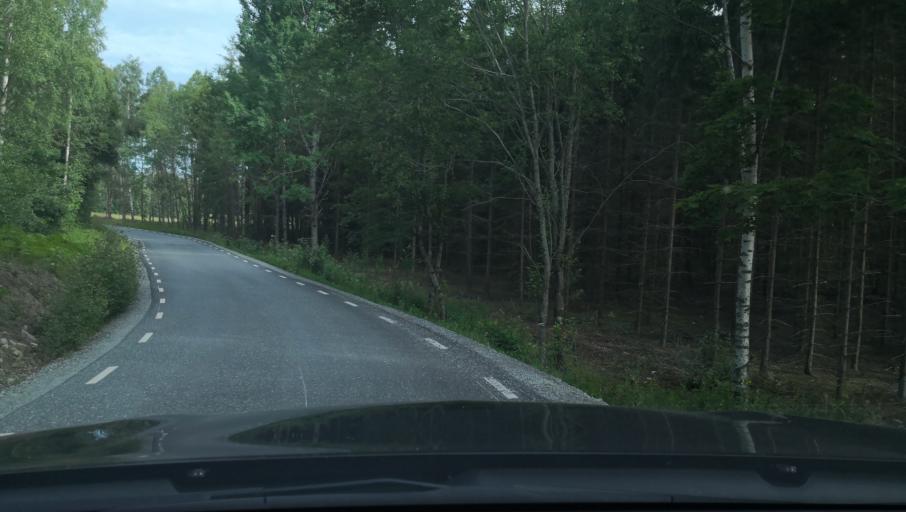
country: SE
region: Vaestmanland
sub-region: Surahammars Kommun
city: Surahammar
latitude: 59.6636
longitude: 16.1668
